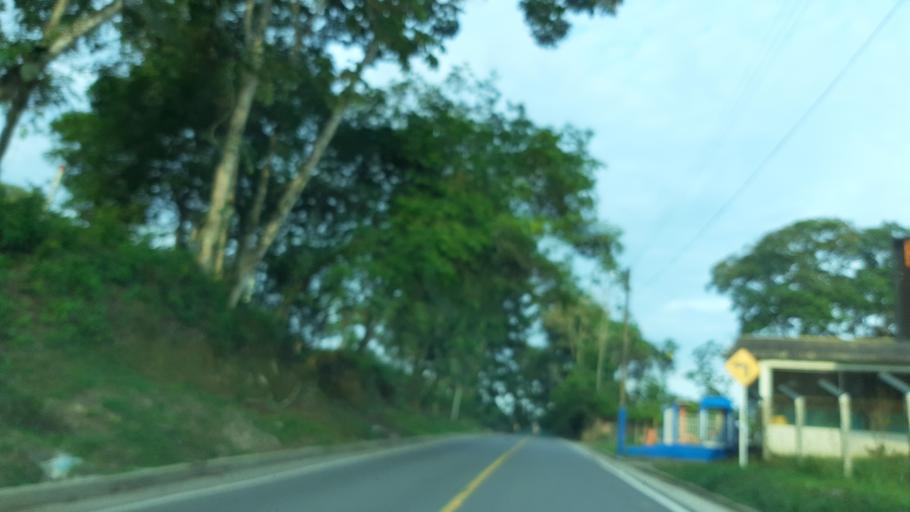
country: CO
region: Boyaca
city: San Luis de Gaceno
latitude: 4.8154
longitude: -73.1762
